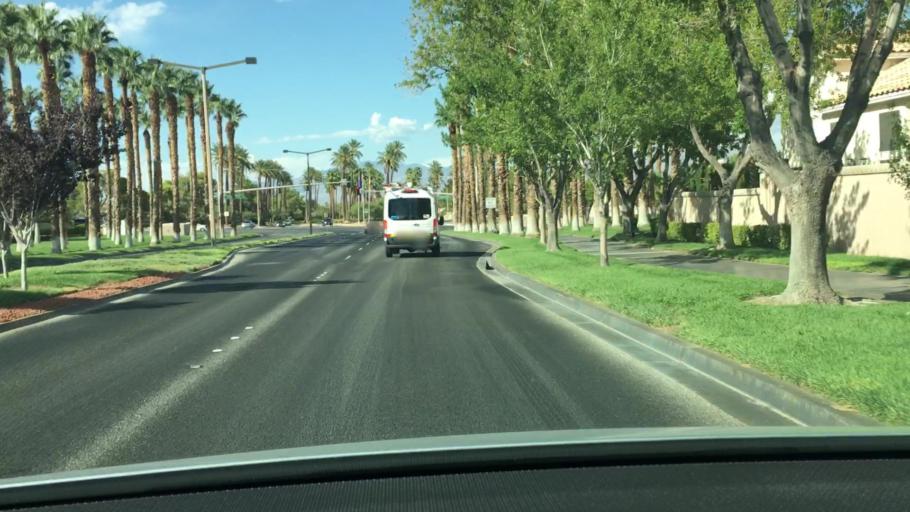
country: US
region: Nevada
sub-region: Clark County
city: Summerlin South
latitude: 36.2047
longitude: -115.3000
